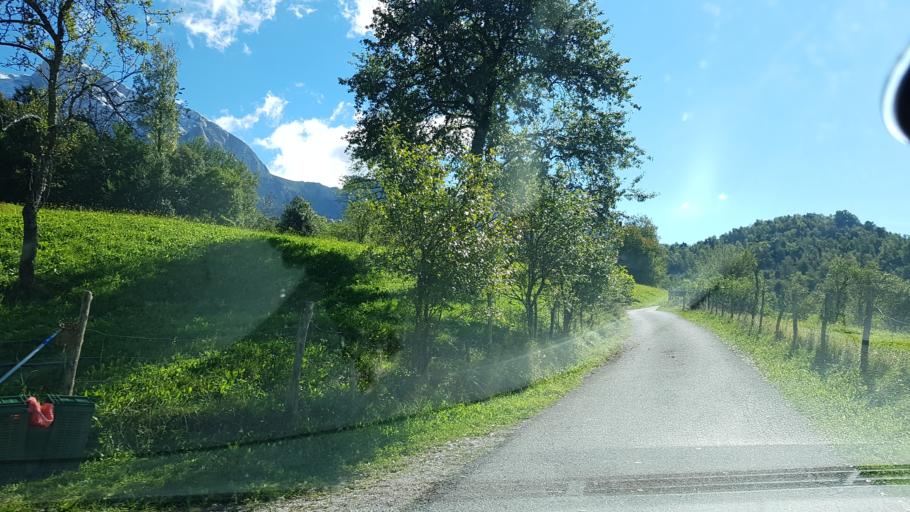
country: SI
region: Kobarid
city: Kobarid
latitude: 46.2698
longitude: 13.6105
